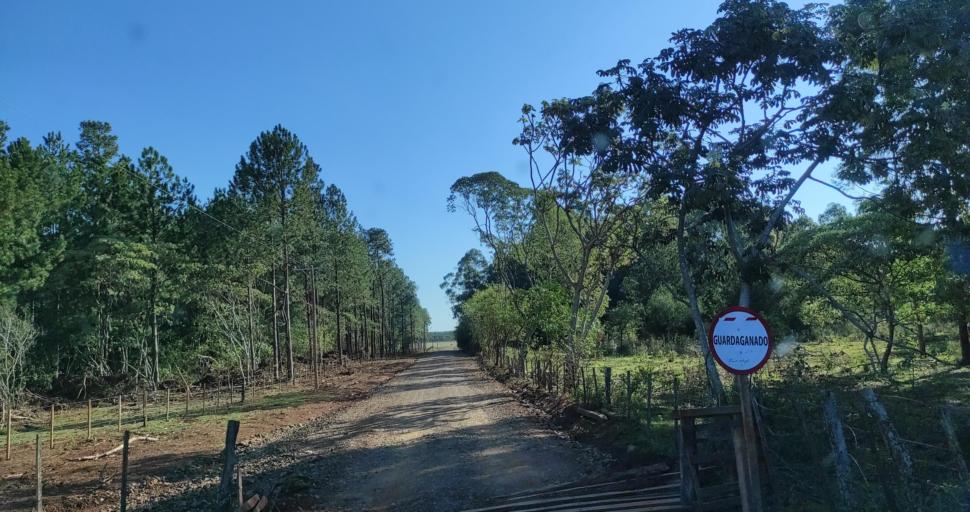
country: PY
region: Itapua
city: San Juan del Parana
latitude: -27.4247
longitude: -56.0923
